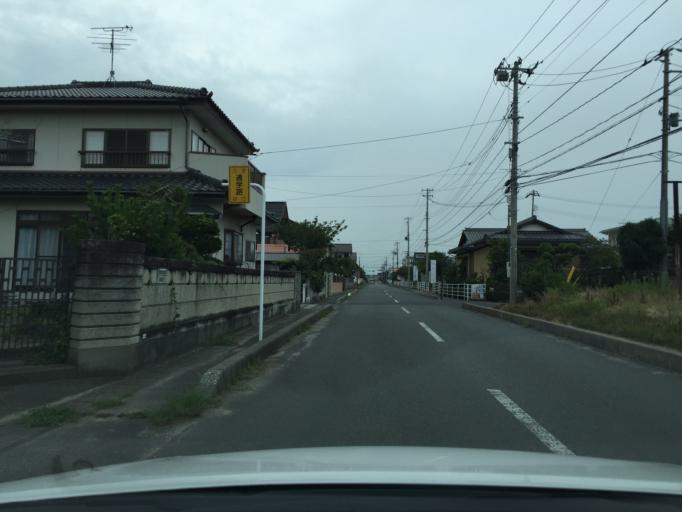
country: JP
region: Fukushima
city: Iwaki
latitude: 37.0157
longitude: 140.9696
